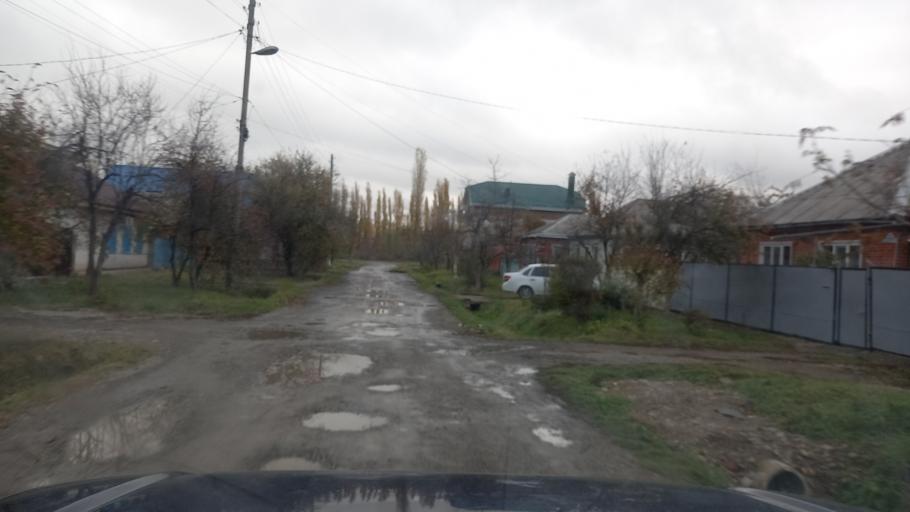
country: RU
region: Adygeya
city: Maykop
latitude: 44.6192
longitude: 40.1288
